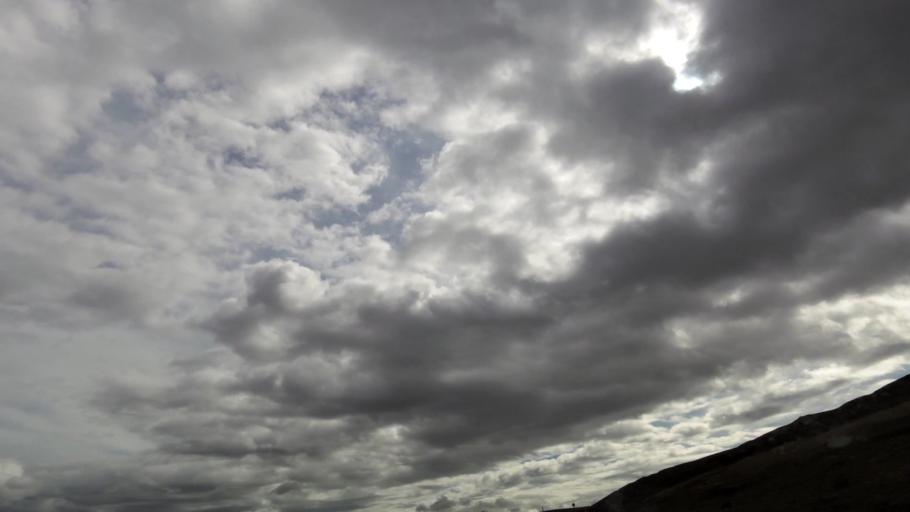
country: IS
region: West
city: Stykkisholmur
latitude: 65.5868
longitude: -22.1530
